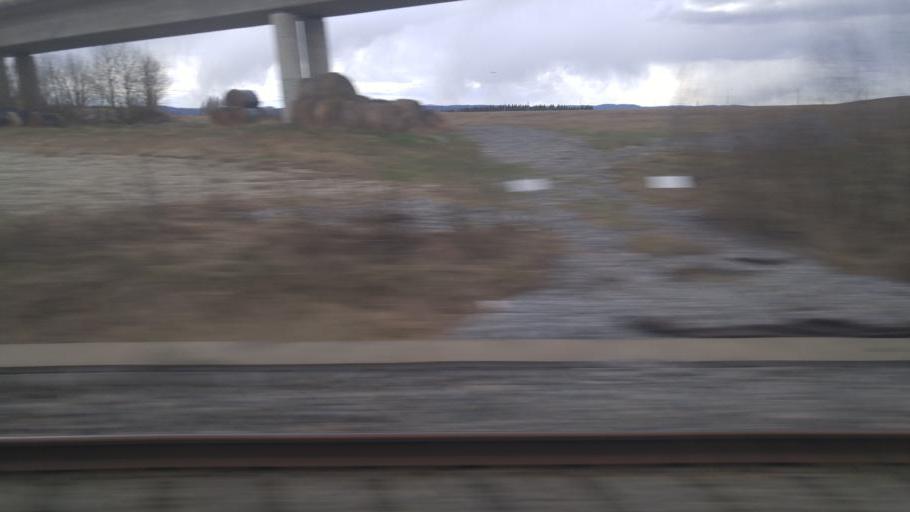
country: NO
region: Akershus
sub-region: Ullensaker
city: Jessheim
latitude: 60.1185
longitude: 11.1563
